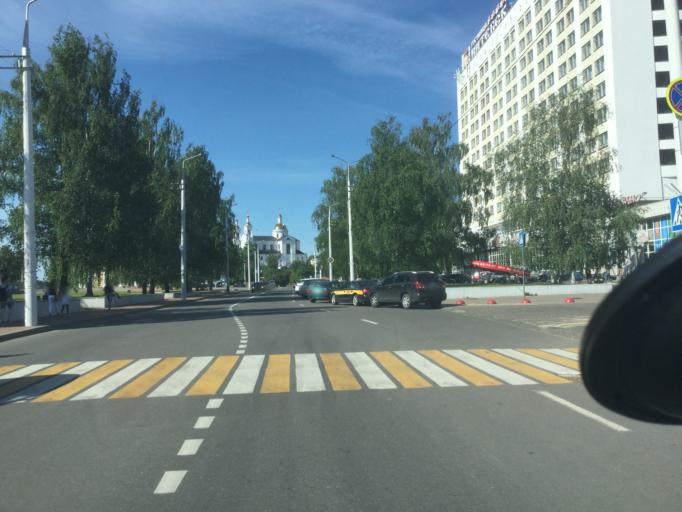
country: BY
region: Vitebsk
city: Vitebsk
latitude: 55.1912
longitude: 30.2017
